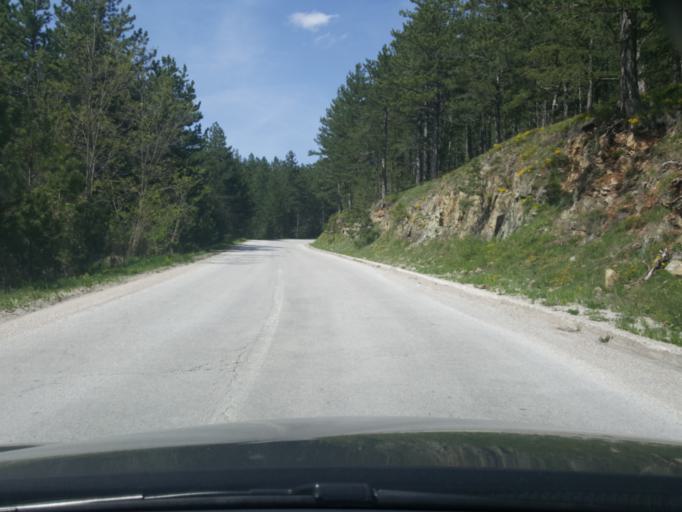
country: RS
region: Central Serbia
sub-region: Zlatiborski Okrug
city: Bajina Basta
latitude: 43.8765
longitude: 19.5658
